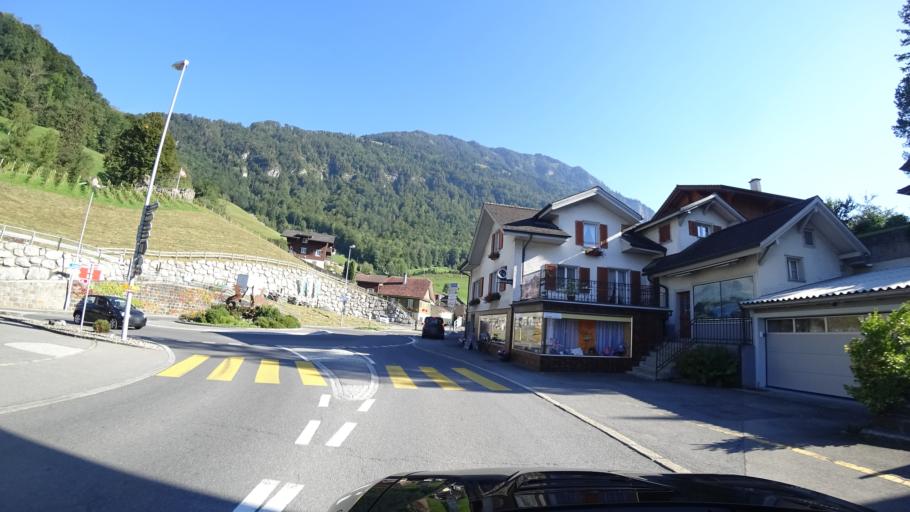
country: CH
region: Obwalden
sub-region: Obwalden
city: Giswil
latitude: 46.8327
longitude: 8.1832
